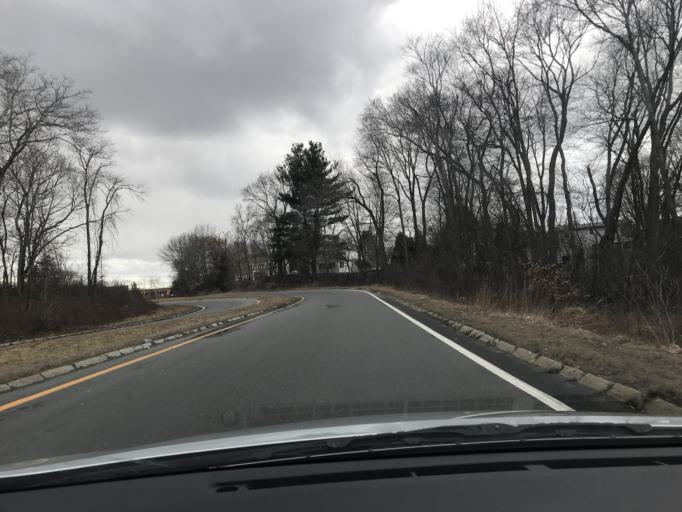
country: US
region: Massachusetts
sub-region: Middlesex County
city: Lexington
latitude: 42.4720
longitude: -71.2438
